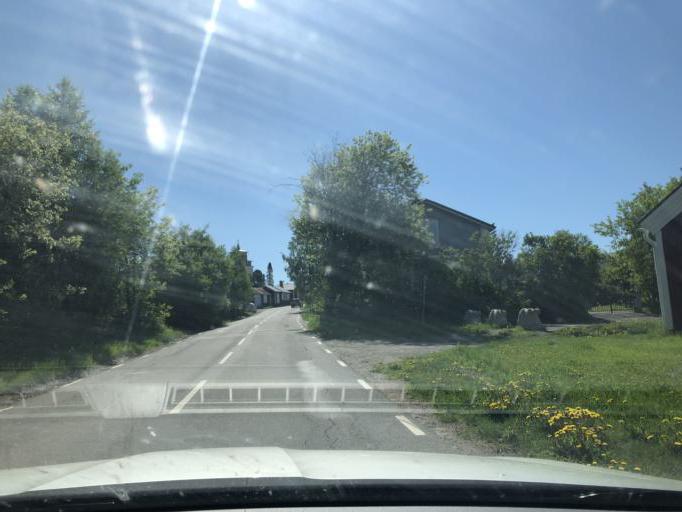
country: SE
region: Norrbotten
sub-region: Lulea Kommun
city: Gammelstad
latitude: 65.6475
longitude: 22.0231
